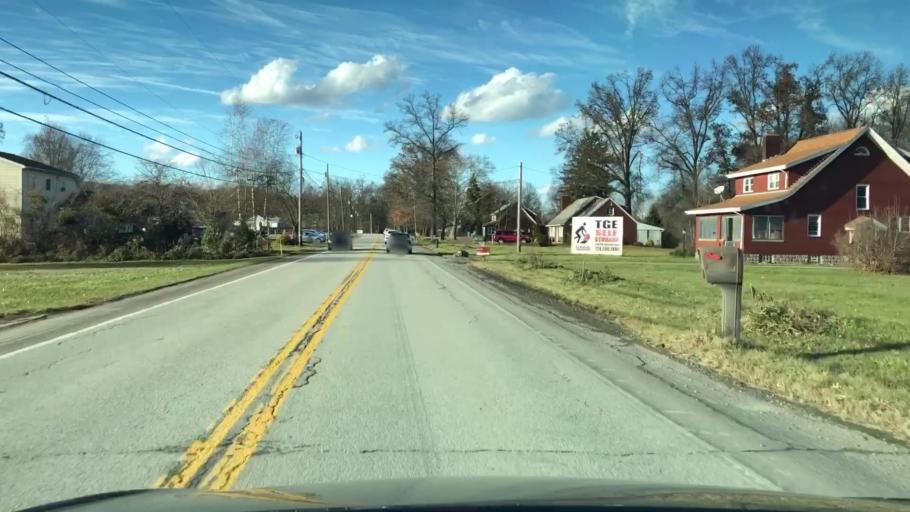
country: US
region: Pennsylvania
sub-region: Butler County
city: Saxonburg
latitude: 40.7459
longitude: -79.7685
